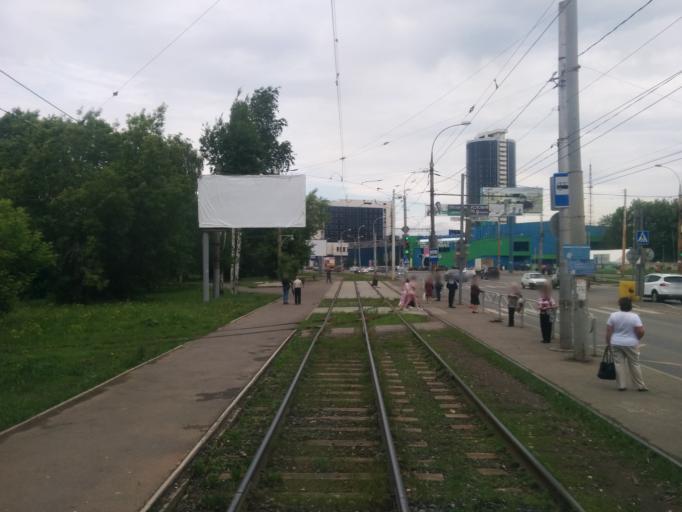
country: RU
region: Perm
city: Perm
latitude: 58.0032
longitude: 56.2863
